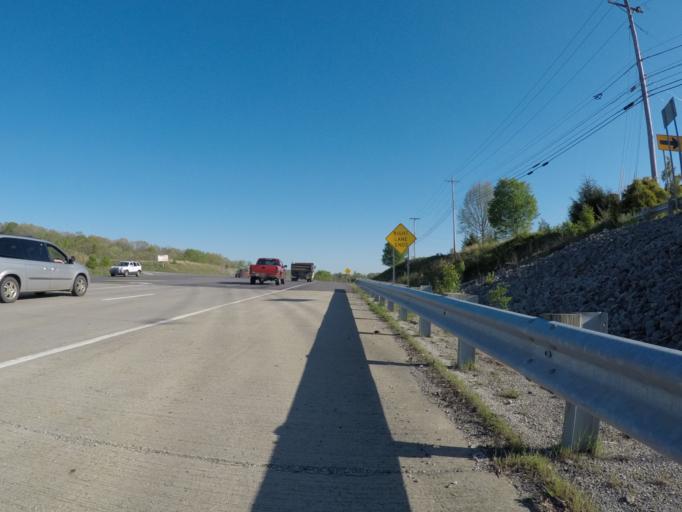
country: US
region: Kentucky
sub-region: Boyd County
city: Meads
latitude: 38.3634
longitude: -82.6986
